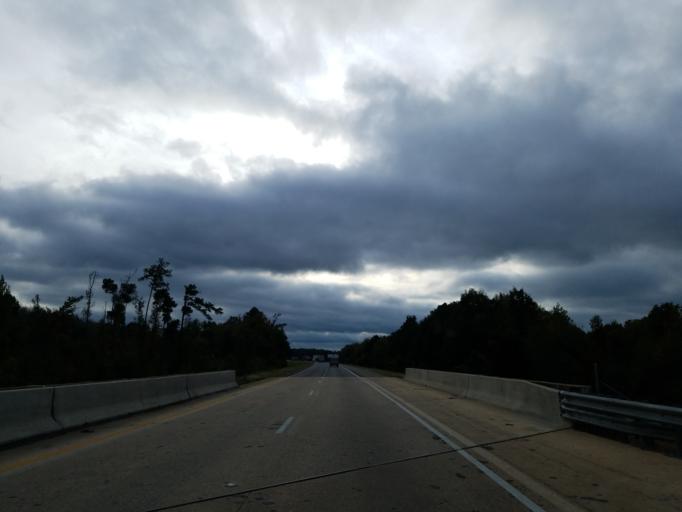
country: US
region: Alabama
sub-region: Tuscaloosa County
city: Tuscaloosa
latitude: 33.1497
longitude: -87.6100
